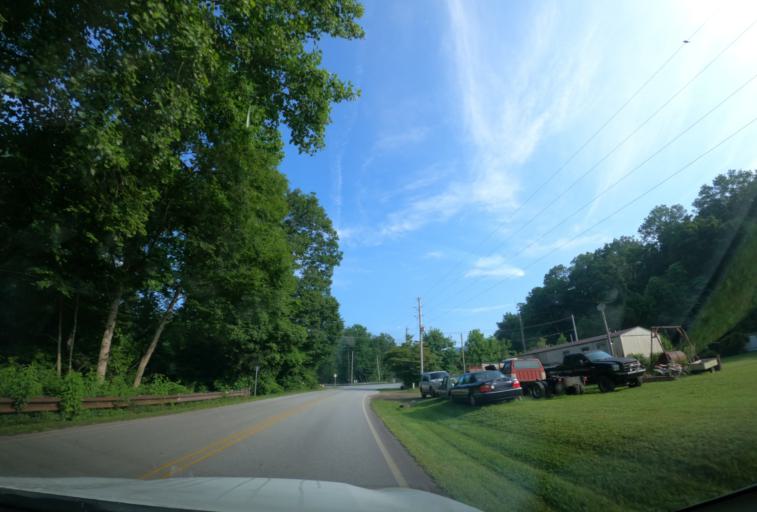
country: US
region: North Carolina
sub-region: Transylvania County
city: Brevard
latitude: 35.2291
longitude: -82.8732
